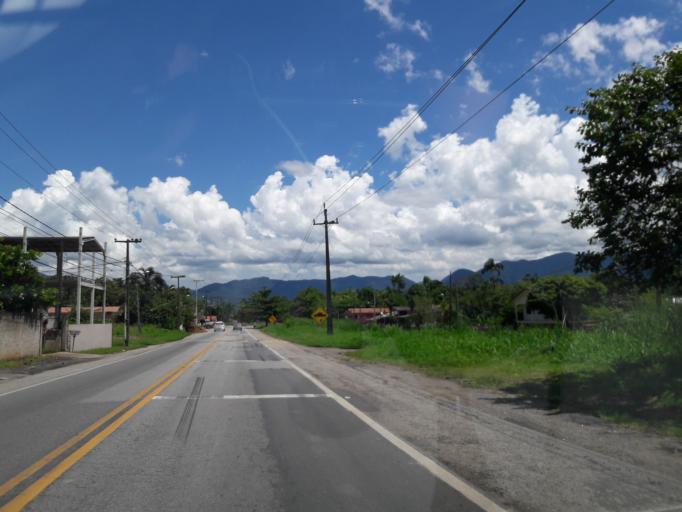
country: BR
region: Parana
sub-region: Antonina
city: Antonina
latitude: -25.4691
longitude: -48.8284
